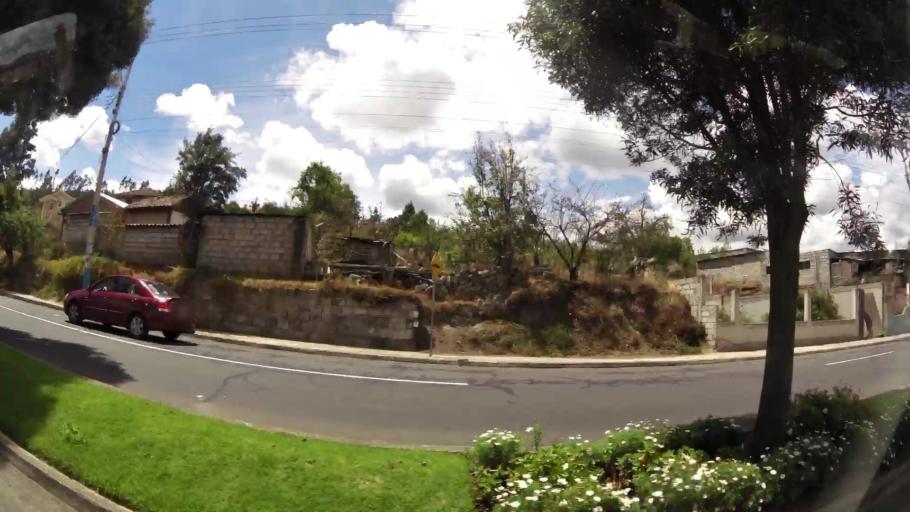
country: EC
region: Tungurahua
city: Ambato
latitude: -1.2776
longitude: -78.6403
